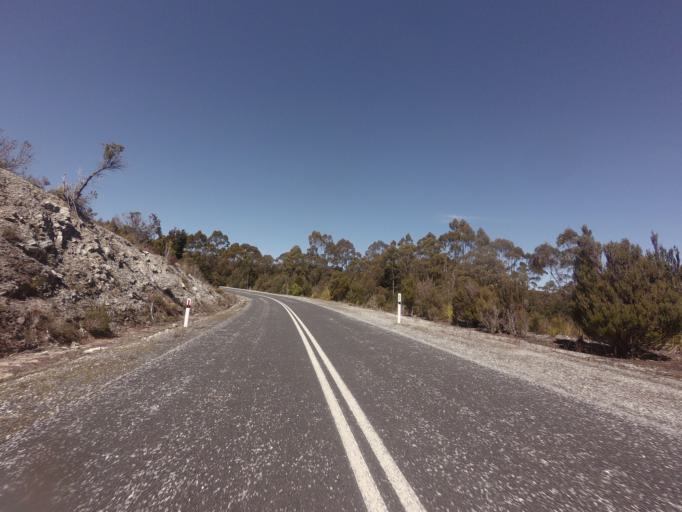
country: AU
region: Tasmania
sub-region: Huon Valley
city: Geeveston
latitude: -42.8219
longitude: 146.1142
